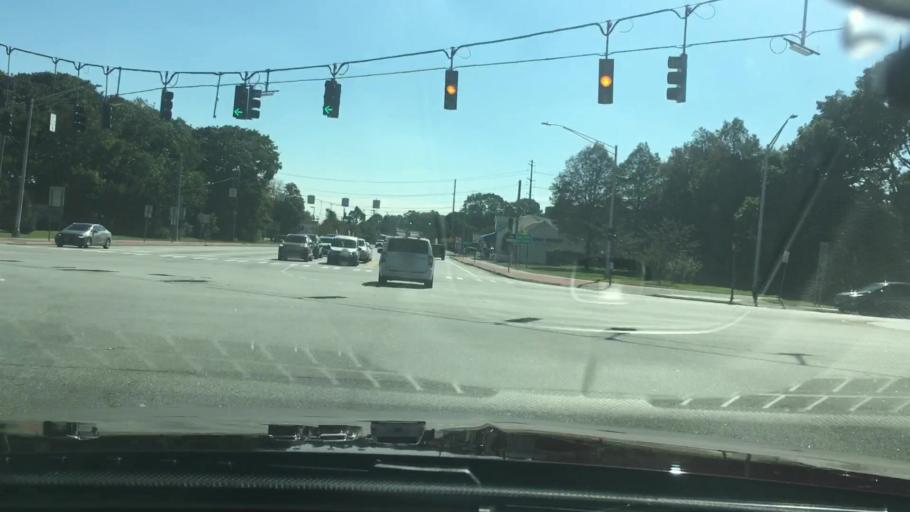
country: US
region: New York
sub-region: Suffolk County
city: Port Jefferson Station
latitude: 40.9252
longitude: -73.0474
